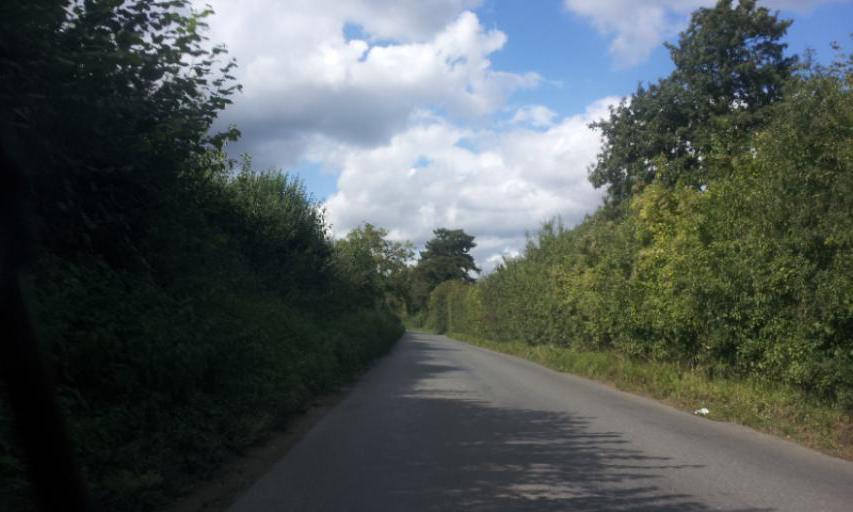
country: GB
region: England
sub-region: Kent
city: West Malling
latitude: 51.3151
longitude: 0.4139
